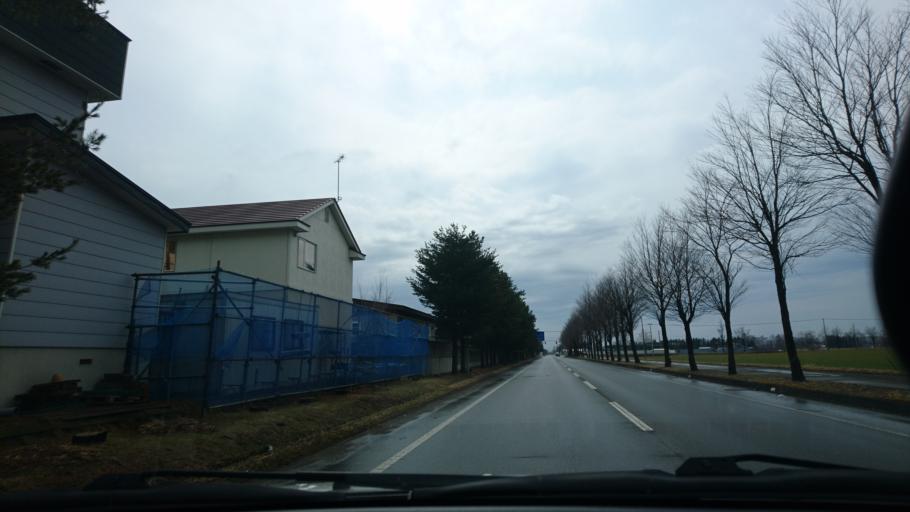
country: JP
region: Hokkaido
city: Otofuke
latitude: 42.9735
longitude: 143.1917
